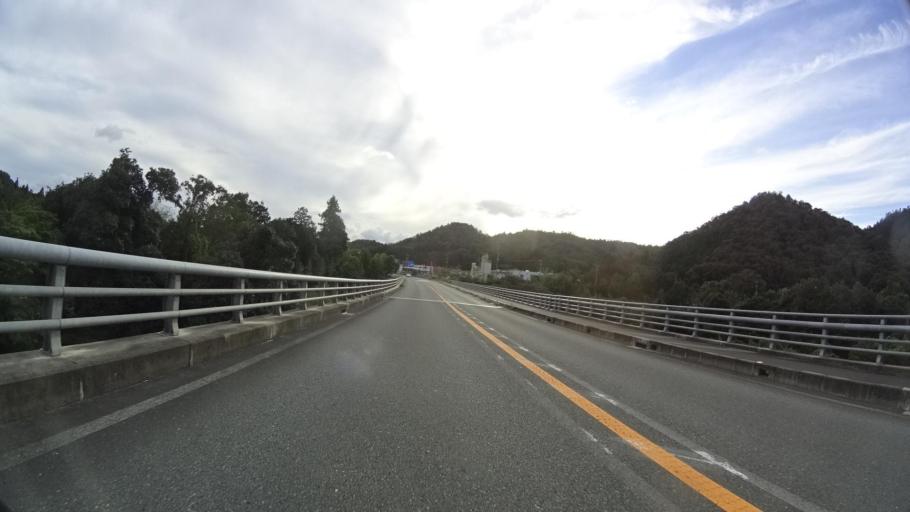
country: JP
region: Kyoto
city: Ayabe
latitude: 35.1985
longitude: 135.4238
